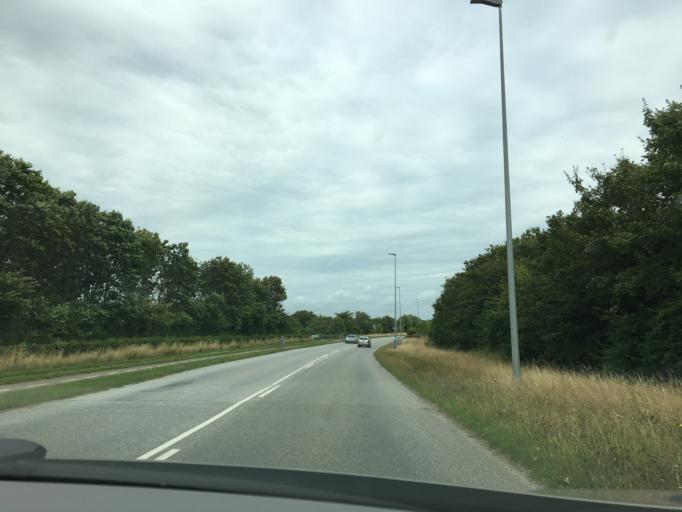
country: DK
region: Central Jutland
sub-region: Ringkobing-Skjern Kommune
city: Ringkobing
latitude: 56.0793
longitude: 8.2693
